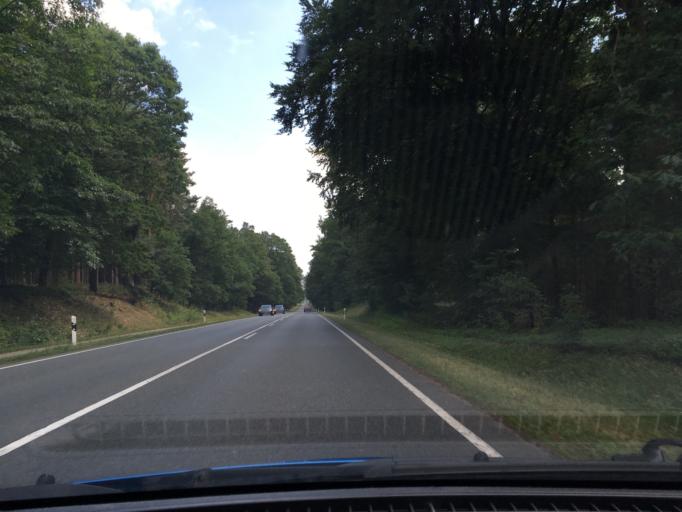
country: DE
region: Lower Saxony
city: Welle
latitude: 53.2732
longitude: 9.7994
